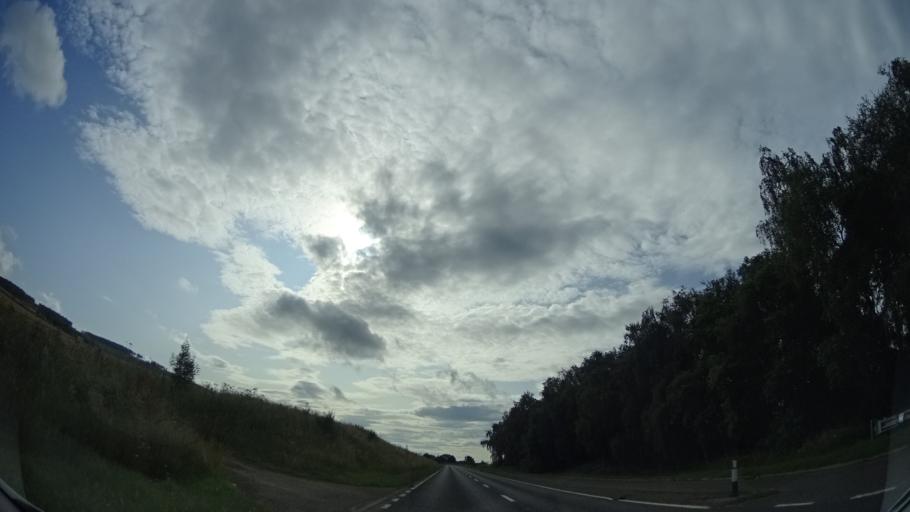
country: GB
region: Scotland
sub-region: Highland
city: Muir of Ord
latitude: 57.5599
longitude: -4.5509
